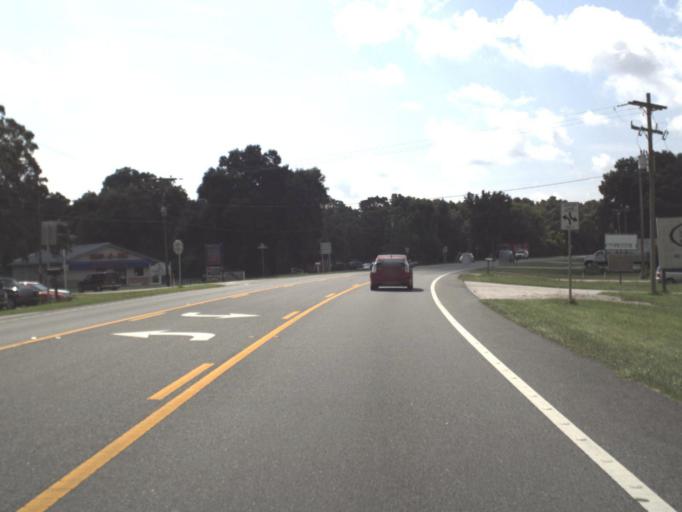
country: US
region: Florida
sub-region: Citrus County
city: Inverness Highlands North
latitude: 28.8598
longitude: -82.3490
